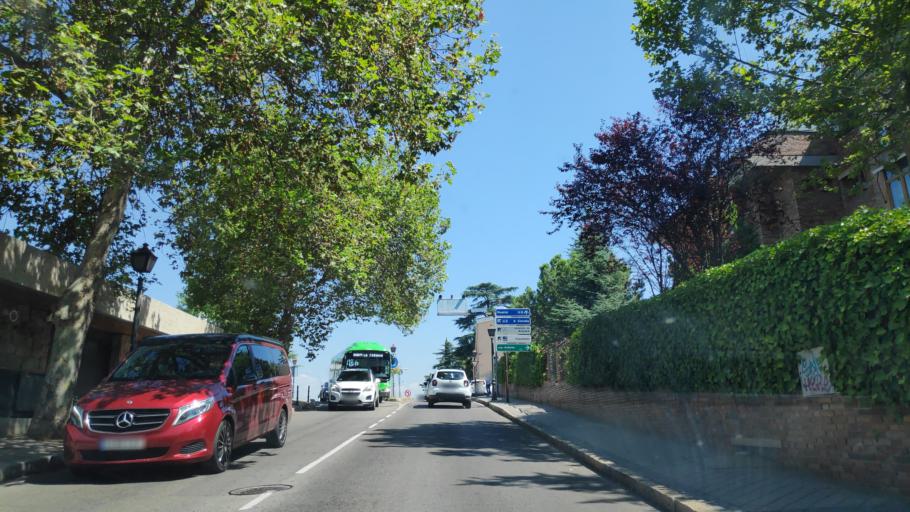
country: ES
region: Madrid
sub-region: Provincia de Madrid
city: Pozuelo de Alarcon
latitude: 40.4615
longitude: -3.7840
